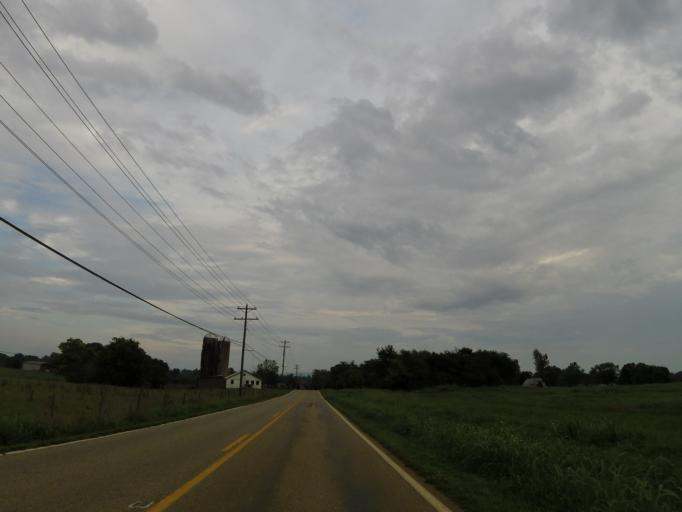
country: US
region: Tennessee
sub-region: Loudon County
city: Greenback
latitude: 35.6572
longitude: -84.1619
